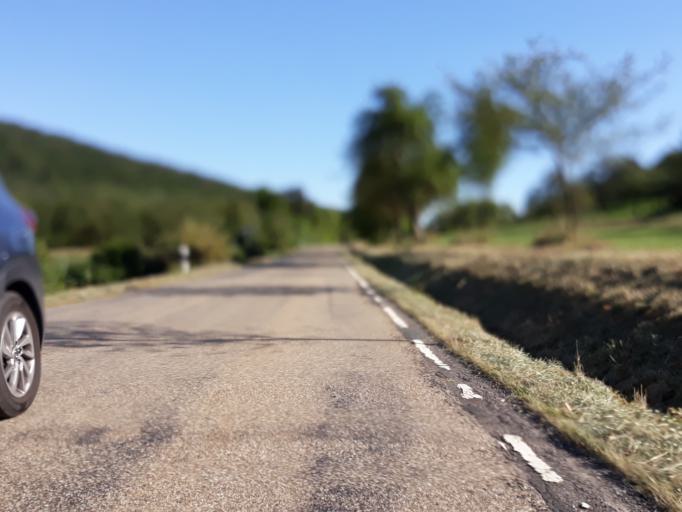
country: DE
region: Baden-Wuerttemberg
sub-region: Regierungsbezirk Stuttgart
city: Aidlingen
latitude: 48.6939
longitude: 8.8976
